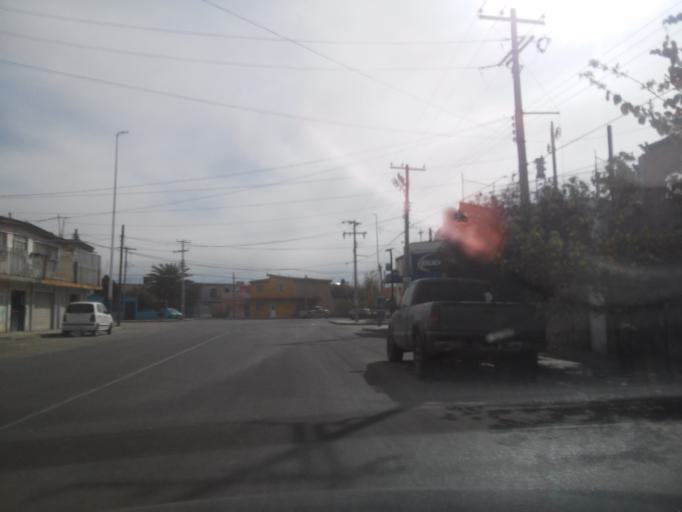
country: MX
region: Durango
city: Victoria de Durango
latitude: 24.0161
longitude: -104.6554
